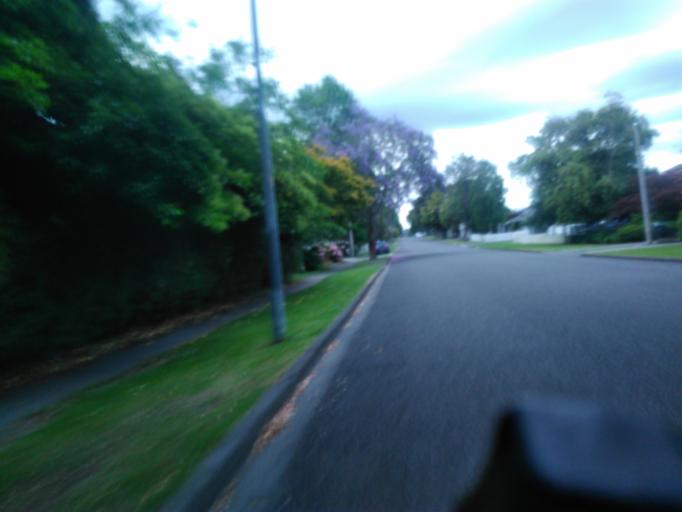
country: NZ
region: Gisborne
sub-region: Gisborne District
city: Gisborne
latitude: -38.6578
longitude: 178.0259
